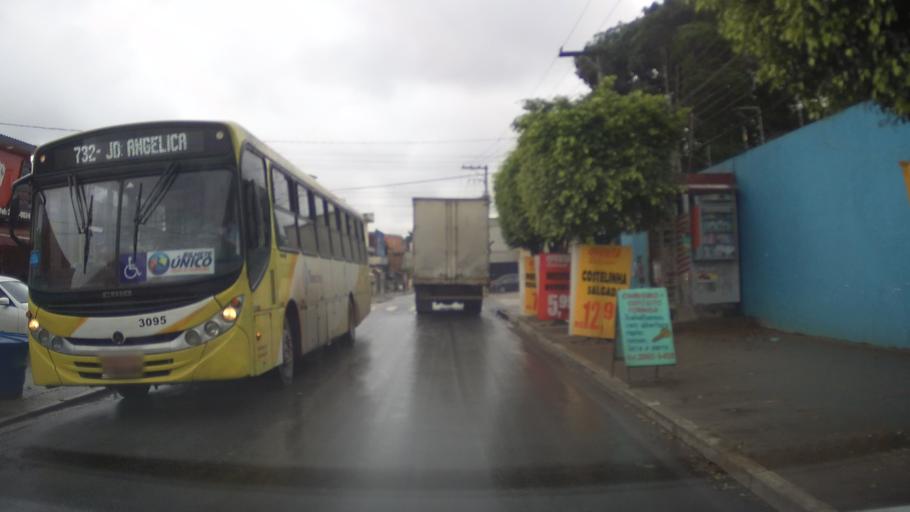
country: BR
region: Sao Paulo
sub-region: Guarulhos
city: Guarulhos
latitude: -23.4746
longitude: -46.4413
